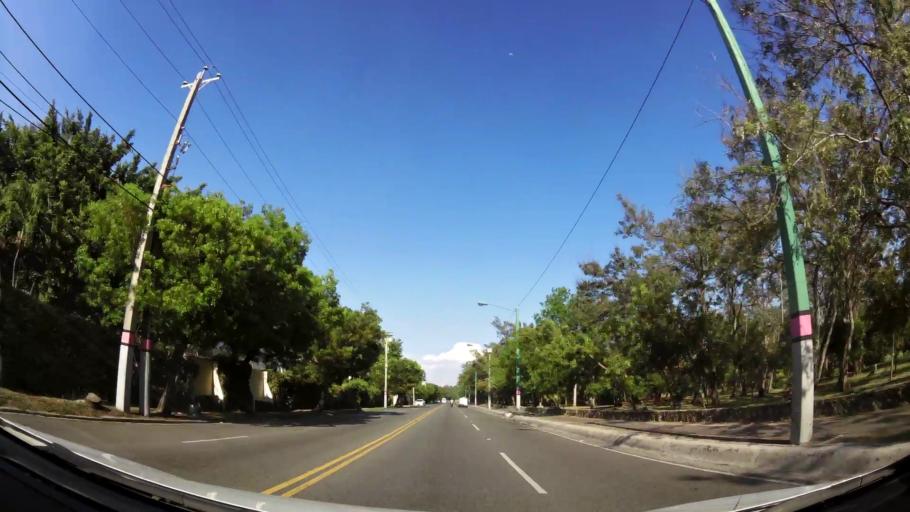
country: DO
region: Nacional
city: Bella Vista
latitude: 18.4439
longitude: -69.9546
